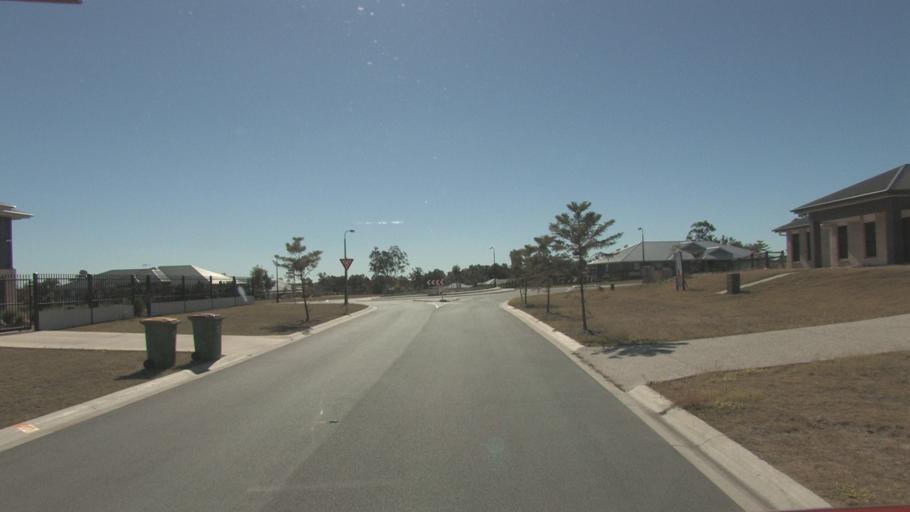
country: AU
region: Queensland
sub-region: Logan
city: North Maclean
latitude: -27.7500
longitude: 152.9467
